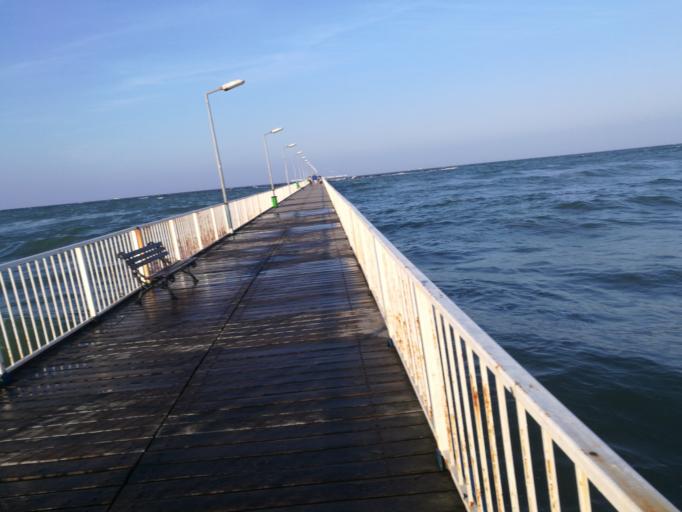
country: RO
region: Constanta
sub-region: Municipiul Constanta
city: Palazu Mare
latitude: 44.2308
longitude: 28.6300
